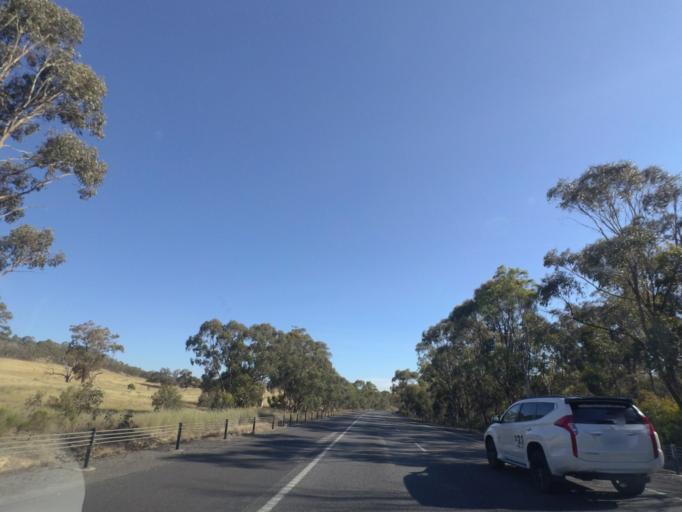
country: AU
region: Victoria
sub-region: Murrindindi
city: Kinglake West
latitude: -37.1654
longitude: 145.0780
